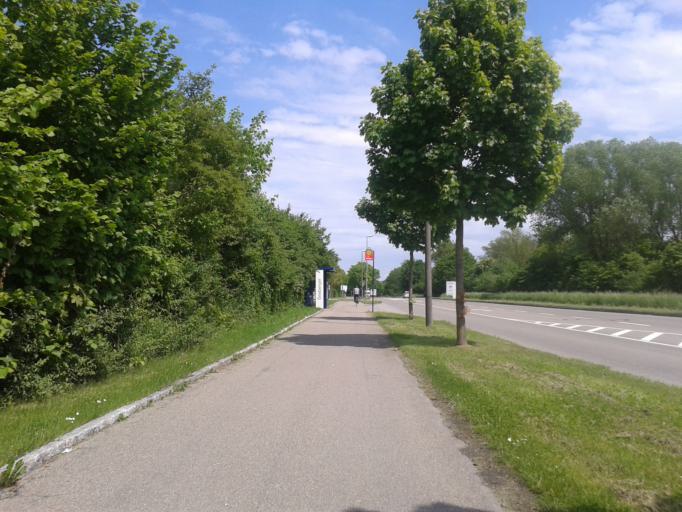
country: DE
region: Baden-Wuerttemberg
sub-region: Tuebingen Region
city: Ulm
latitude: 48.3582
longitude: 9.9501
